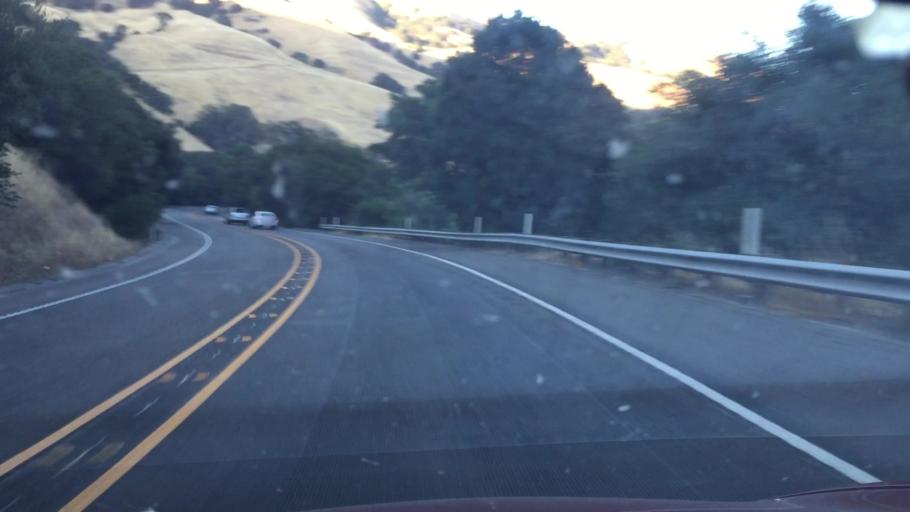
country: US
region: California
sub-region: Alameda County
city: Fremont
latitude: 37.5969
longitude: -121.9282
